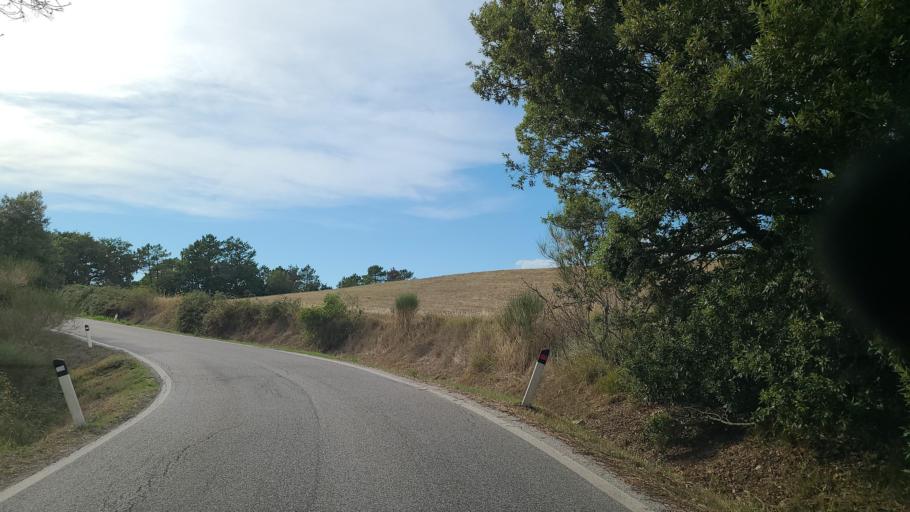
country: IT
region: Tuscany
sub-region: Provincia di Siena
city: San Gimignano
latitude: 43.4280
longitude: 10.9719
